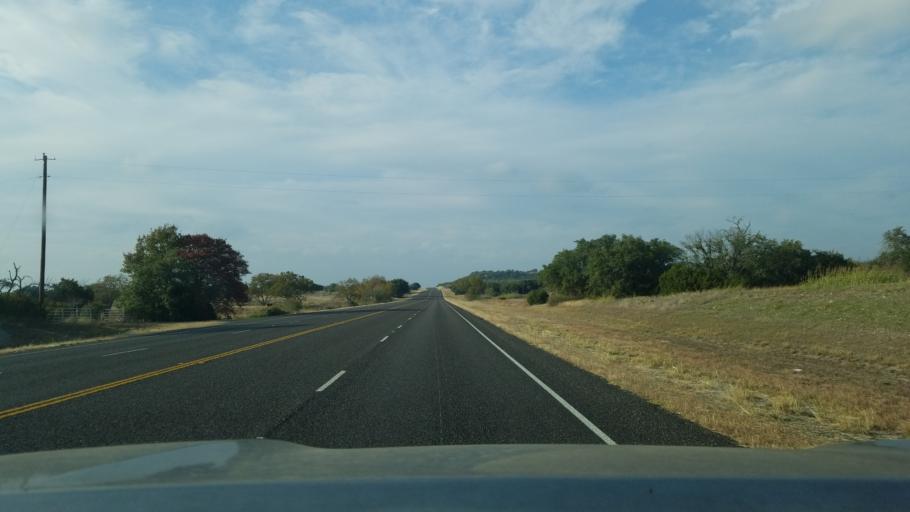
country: US
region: Texas
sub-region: Mills County
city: Goldthwaite
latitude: 31.2490
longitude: -98.4284
